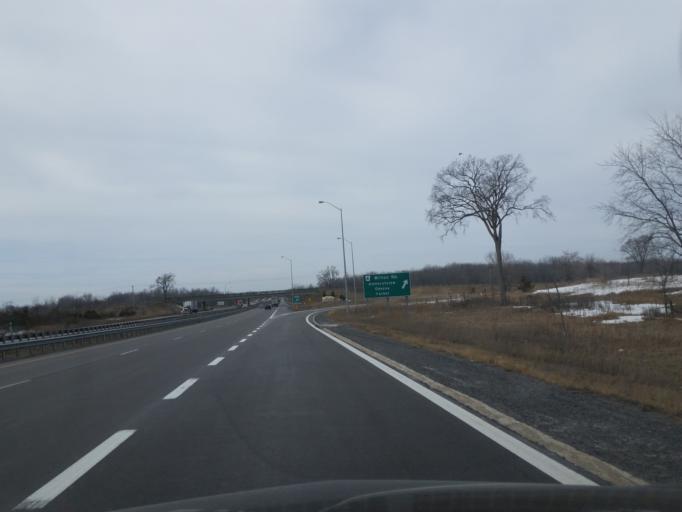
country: CA
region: Ontario
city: Skatepark
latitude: 44.2829
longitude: -76.7115
